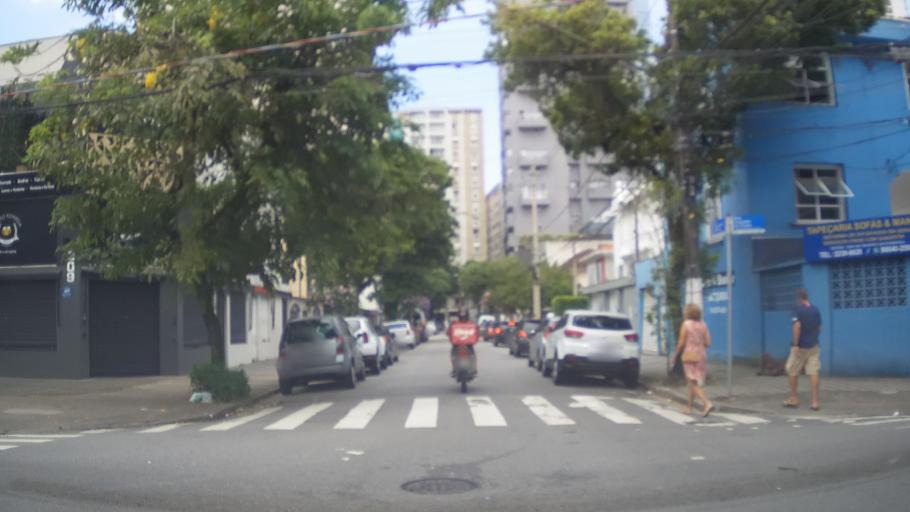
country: BR
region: Sao Paulo
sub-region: Santos
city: Santos
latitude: -23.9652
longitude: -46.3410
